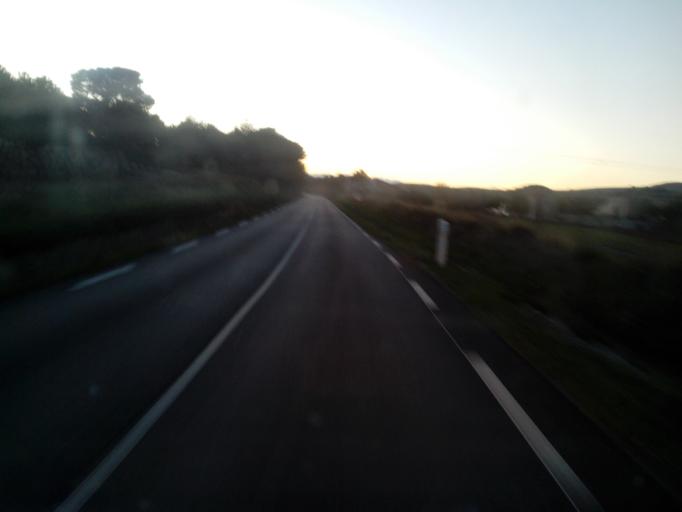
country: FR
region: Languedoc-Roussillon
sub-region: Departement des Pyrenees-Orientales
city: Baixas
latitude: 42.7823
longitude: 2.7980
